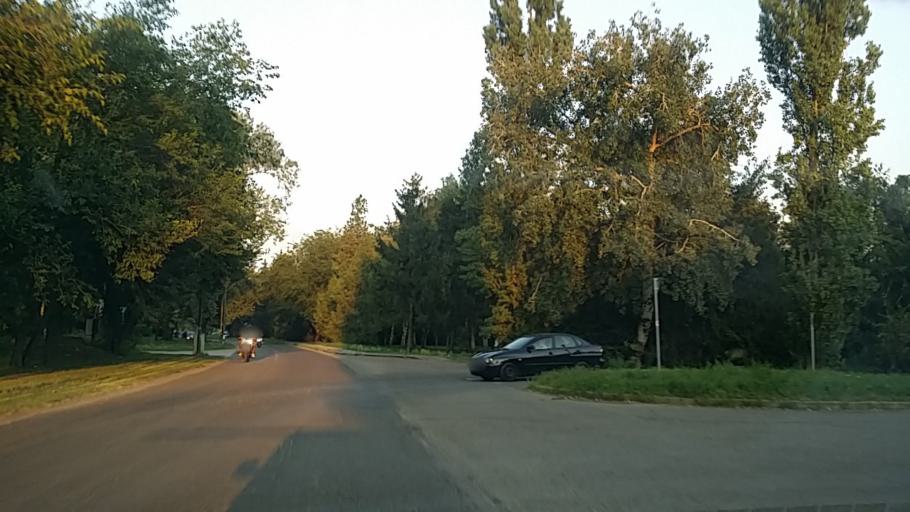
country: HU
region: Fejer
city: Dunaujvaros
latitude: 46.9815
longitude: 18.9429
